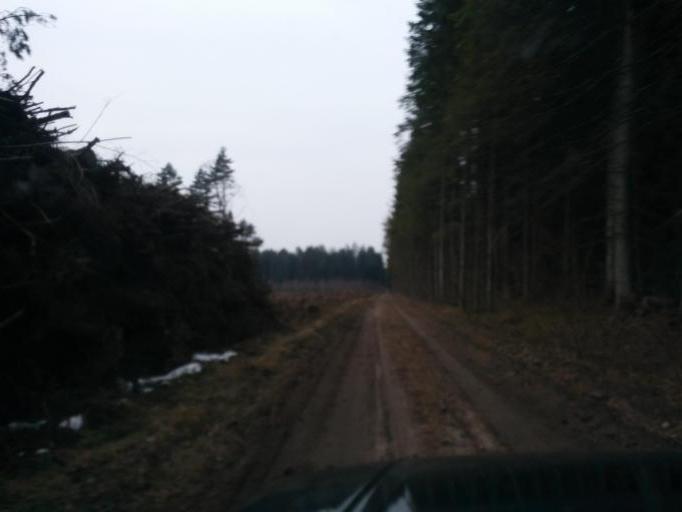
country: LV
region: Ikskile
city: Ikskile
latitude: 56.8098
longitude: 24.4817
